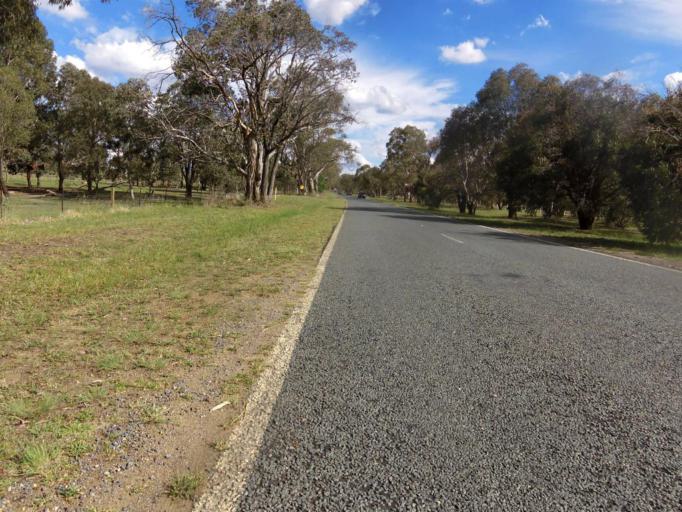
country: AU
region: Australian Capital Territory
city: Belconnen
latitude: -35.1766
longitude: 149.0719
